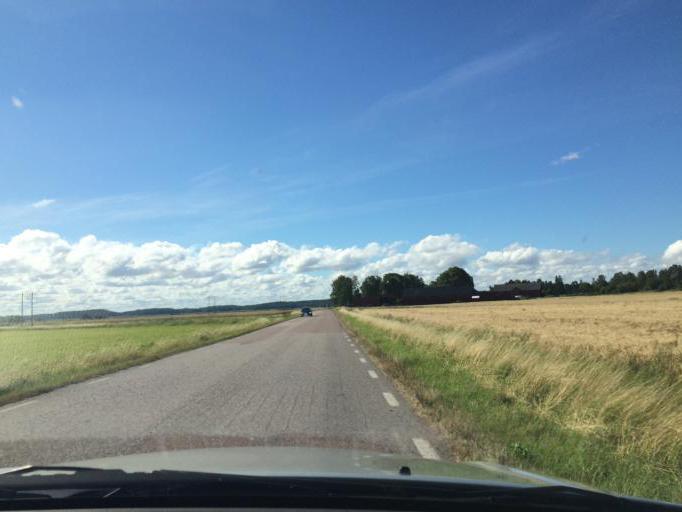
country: SE
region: Soedermanland
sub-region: Eskilstuna Kommun
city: Torshalla
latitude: 59.5370
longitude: 16.4479
